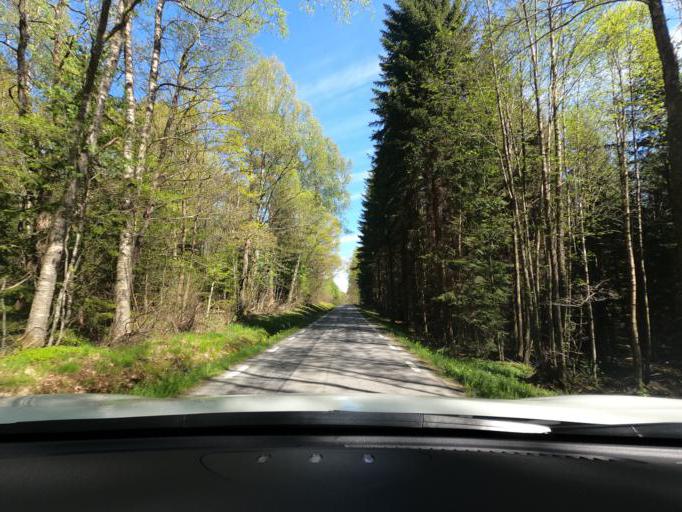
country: SE
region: Vaestra Goetaland
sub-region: Marks Kommun
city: Horred
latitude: 57.4326
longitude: 12.4121
